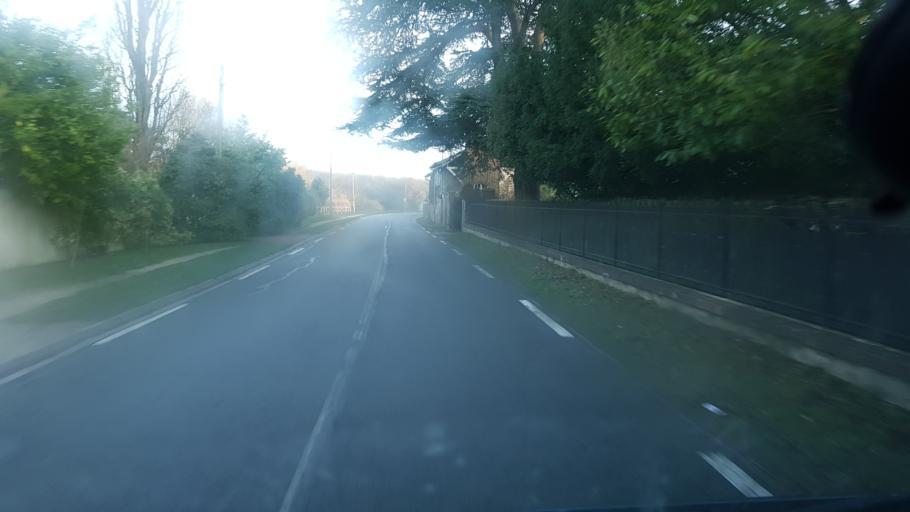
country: FR
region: Ile-de-France
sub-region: Departement des Yvelines
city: Le Perray-en-Yvelines
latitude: 48.6873
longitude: 1.8668
